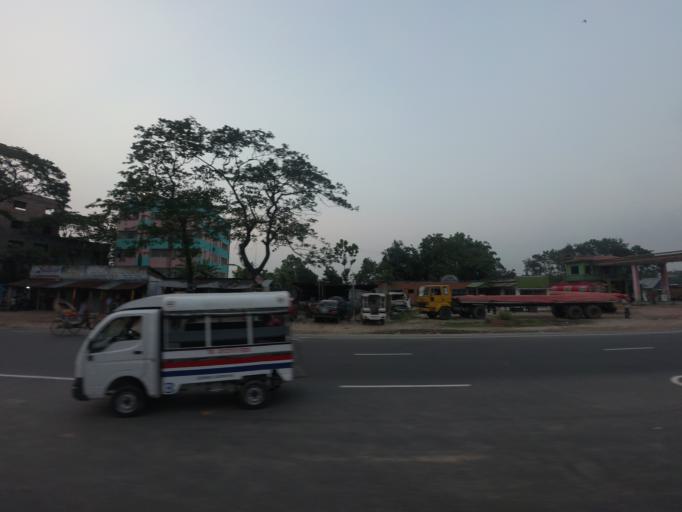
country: BD
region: Chittagong
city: Comilla
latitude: 23.4779
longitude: 91.1057
